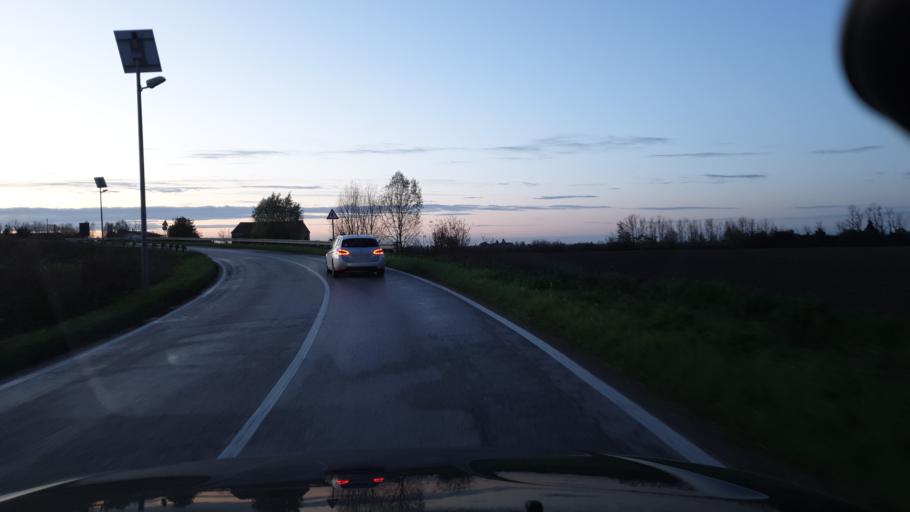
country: IT
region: Veneto
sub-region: Provincia di Rovigo
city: Fratta Polesine
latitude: 45.0215
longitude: 11.6373
